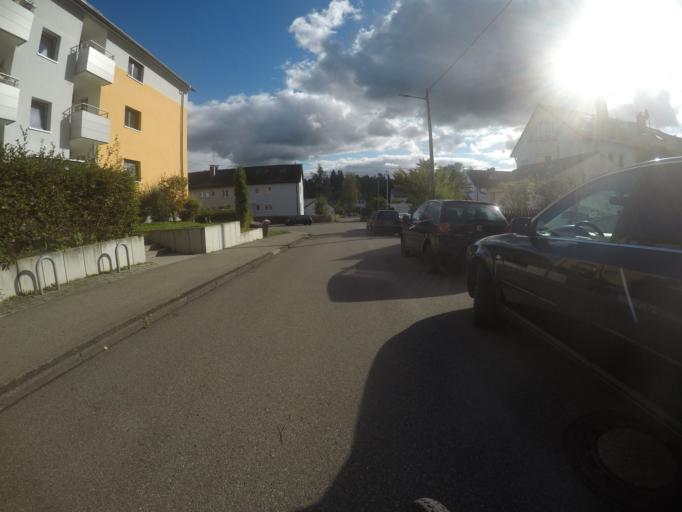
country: DE
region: Baden-Wuerttemberg
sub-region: Regierungsbezirk Stuttgart
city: Gerlingen
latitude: 48.7492
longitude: 9.0741
